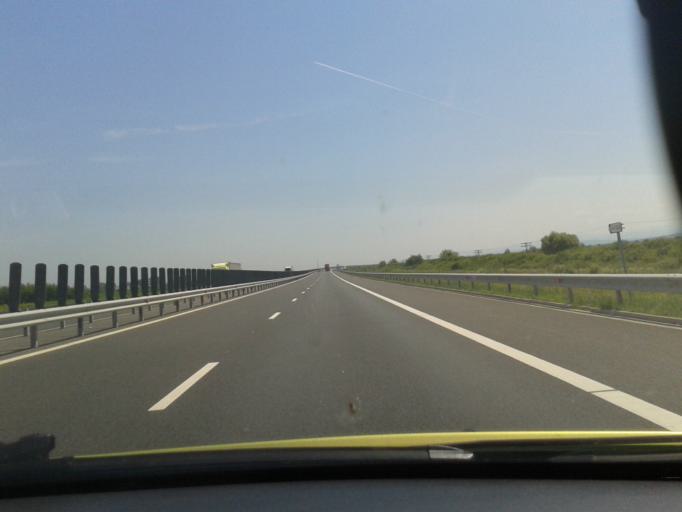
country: RO
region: Timis
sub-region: Comuna Balint
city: Balint
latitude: 45.8009
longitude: 21.8775
